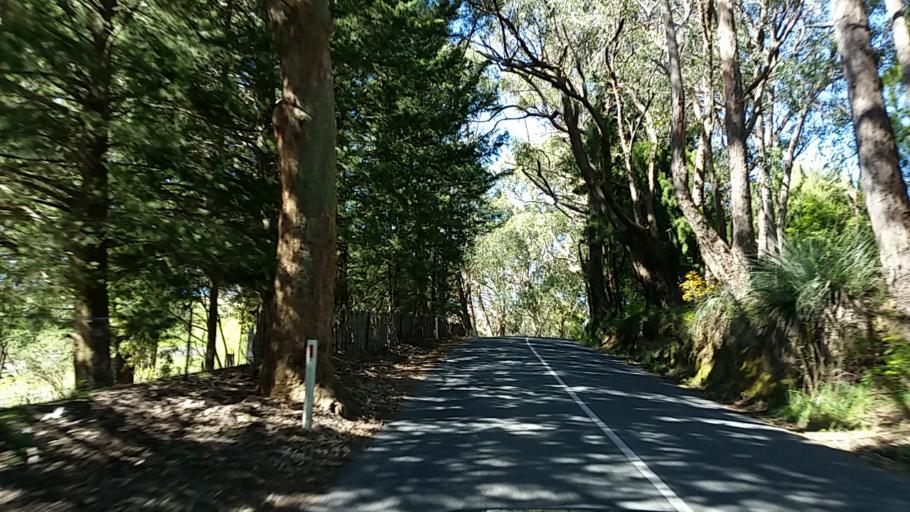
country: AU
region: South Australia
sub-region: Adelaide Hills
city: Bridgewater
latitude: -34.9567
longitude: 138.7503
